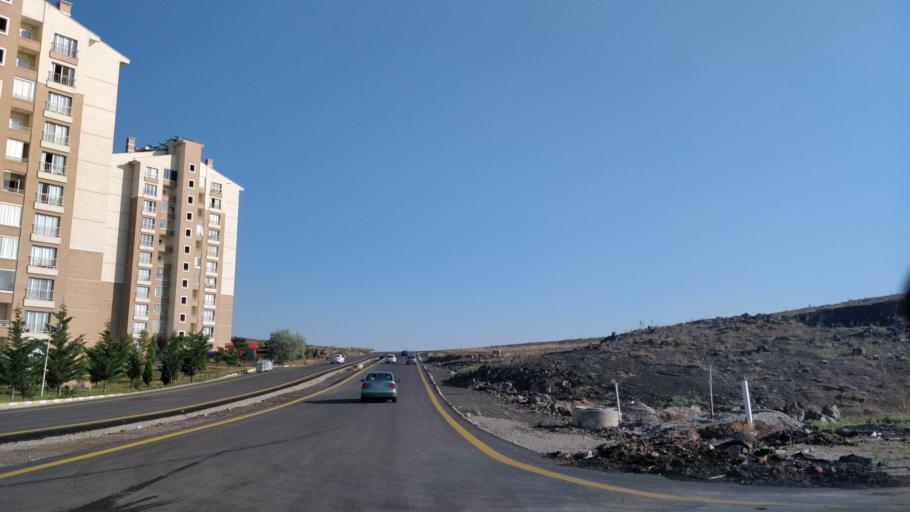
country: TR
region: Ankara
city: Etimesgut
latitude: 39.8444
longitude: 32.5462
